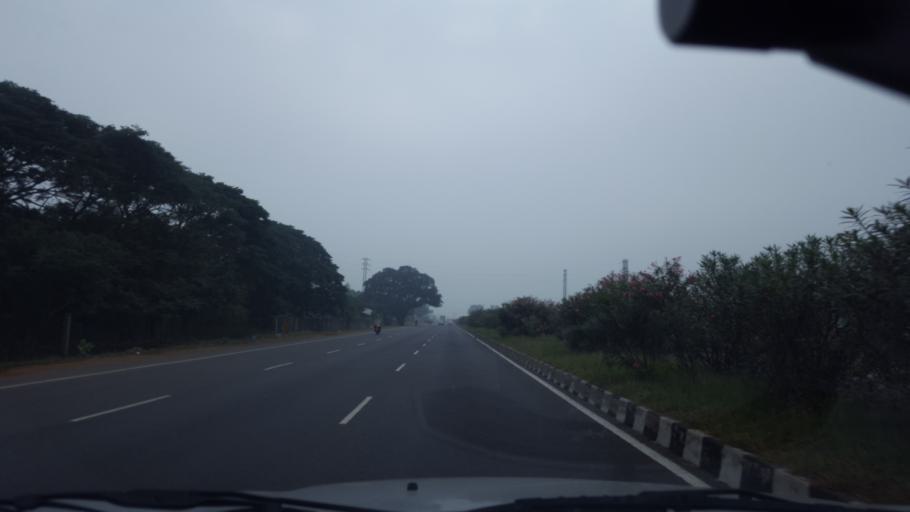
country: IN
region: Andhra Pradesh
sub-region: Prakasam
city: Ongole
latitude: 15.6063
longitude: 80.0279
